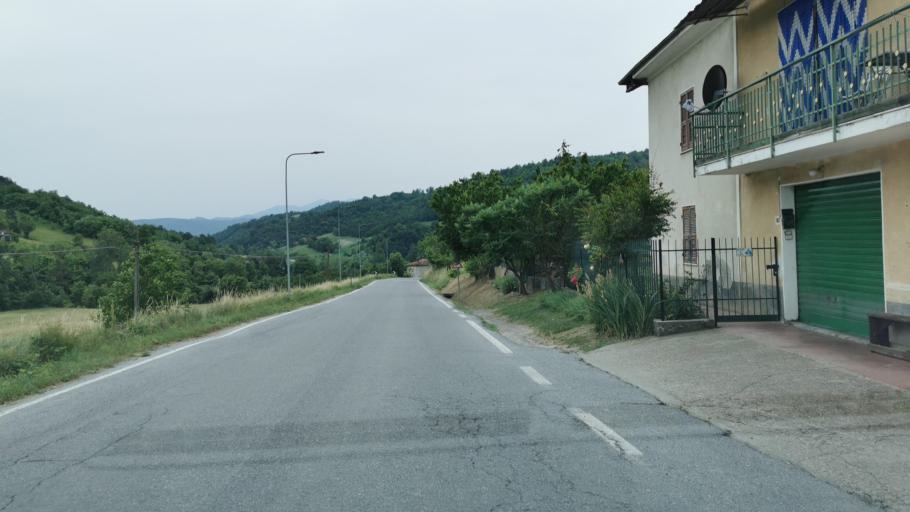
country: IT
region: Piedmont
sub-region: Provincia di Cuneo
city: Torresina
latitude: 44.4201
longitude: 8.0517
